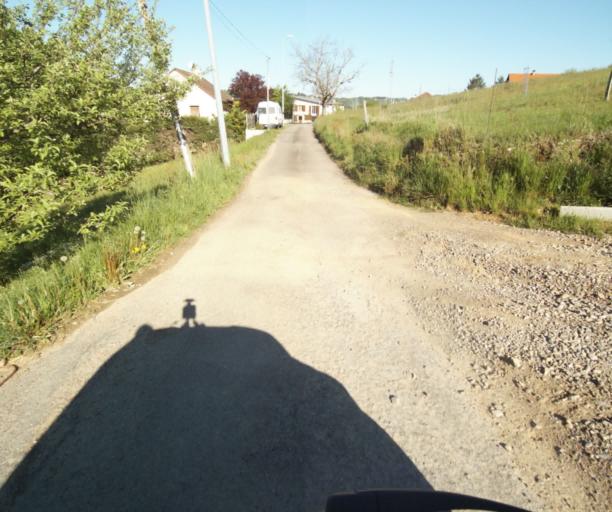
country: FR
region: Limousin
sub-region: Departement de la Correze
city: Tulle
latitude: 45.2647
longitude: 1.7834
